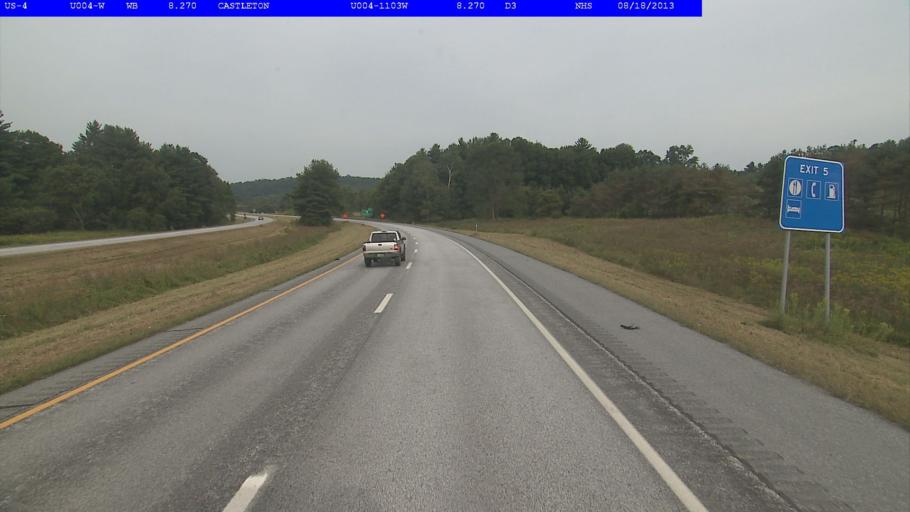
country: US
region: Vermont
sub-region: Rutland County
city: Castleton
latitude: 43.6165
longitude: -73.1548
